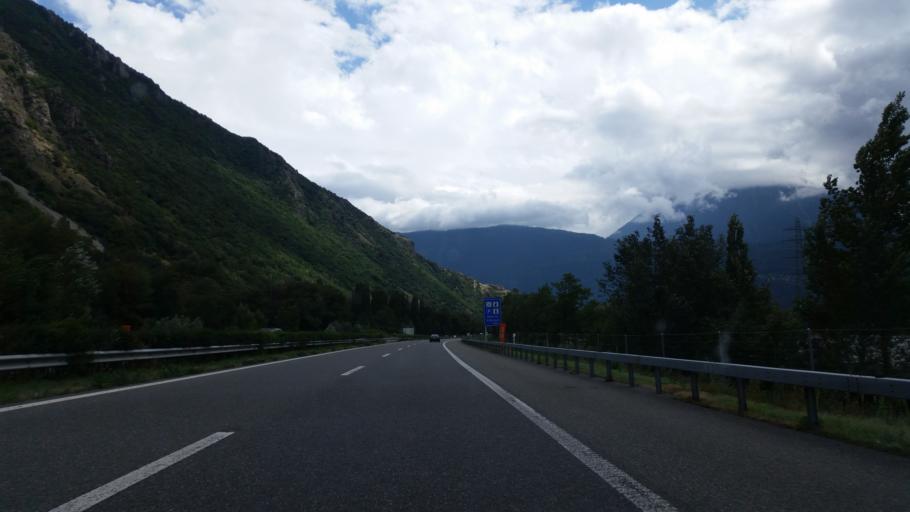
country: CH
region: Valais
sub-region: Saint-Maurice District
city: Vernayaz
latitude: 46.1347
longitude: 7.0521
